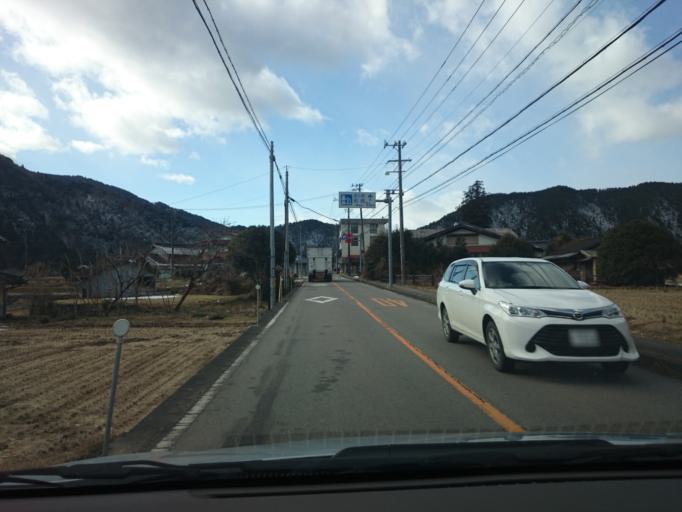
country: JP
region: Gifu
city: Gujo
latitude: 35.7441
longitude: 137.0770
